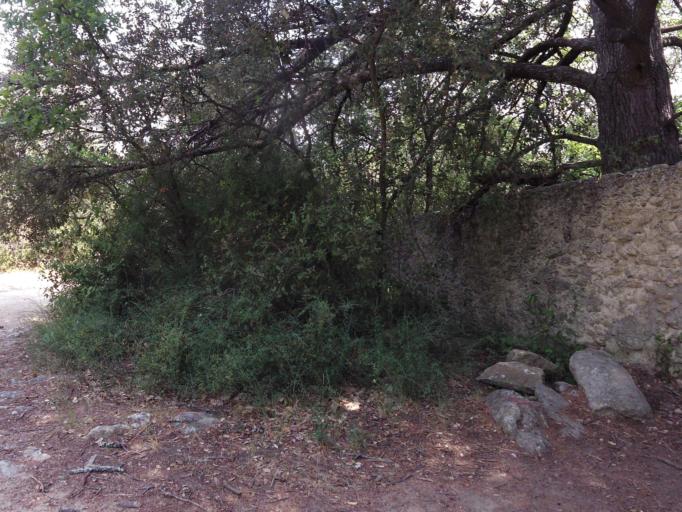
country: FR
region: Languedoc-Roussillon
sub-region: Departement du Gard
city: Aubais
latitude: 43.7609
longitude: 4.1333
